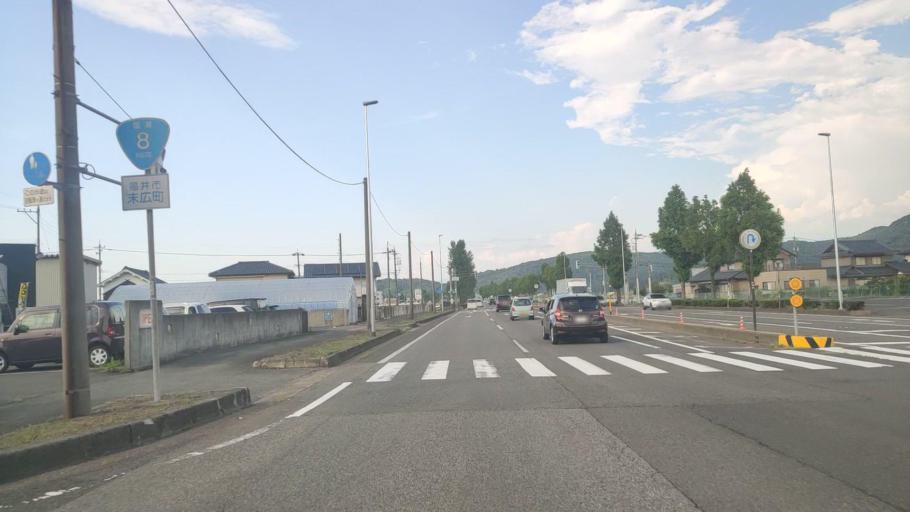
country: JP
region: Fukui
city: Sabae
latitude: 35.9901
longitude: 136.2005
